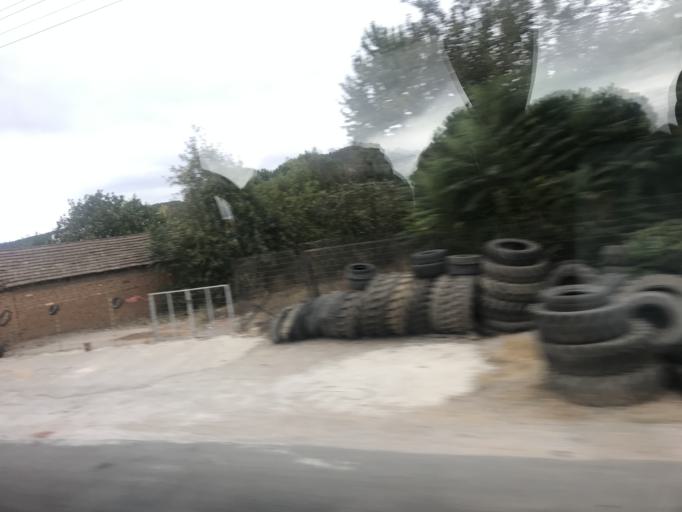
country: TR
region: Balikesir
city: Ergama
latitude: 39.6296
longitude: 27.6251
